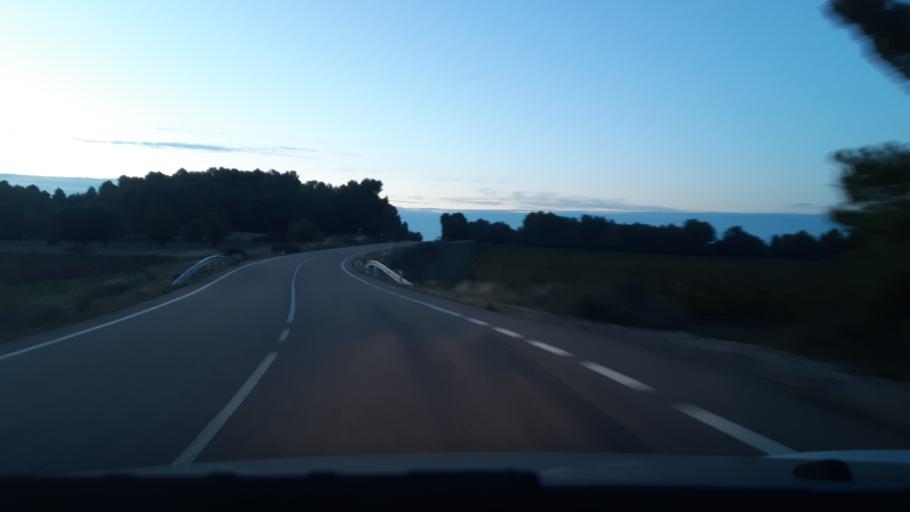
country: ES
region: Aragon
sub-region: Provincia de Teruel
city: Lledo
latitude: 40.9535
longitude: 0.2226
